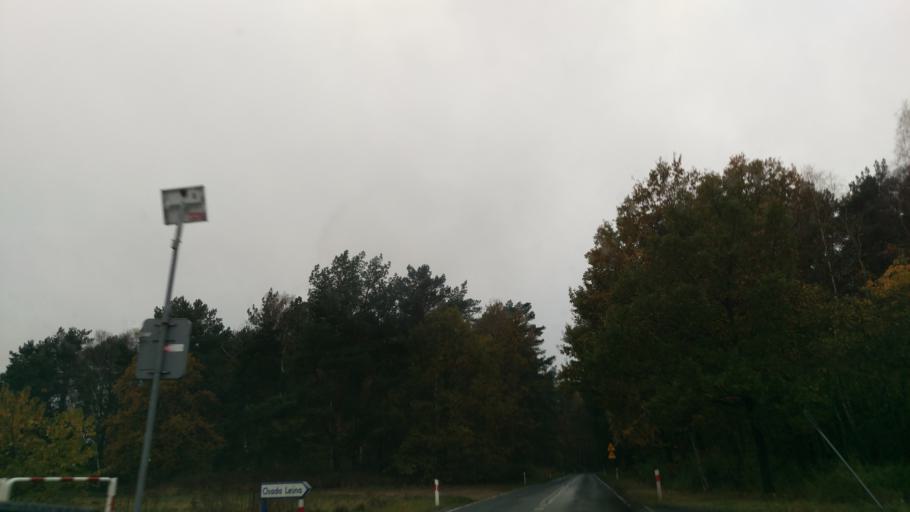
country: PL
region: West Pomeranian Voivodeship
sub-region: Powiat gryfinski
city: Stare Czarnowo
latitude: 53.3937
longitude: 14.7459
